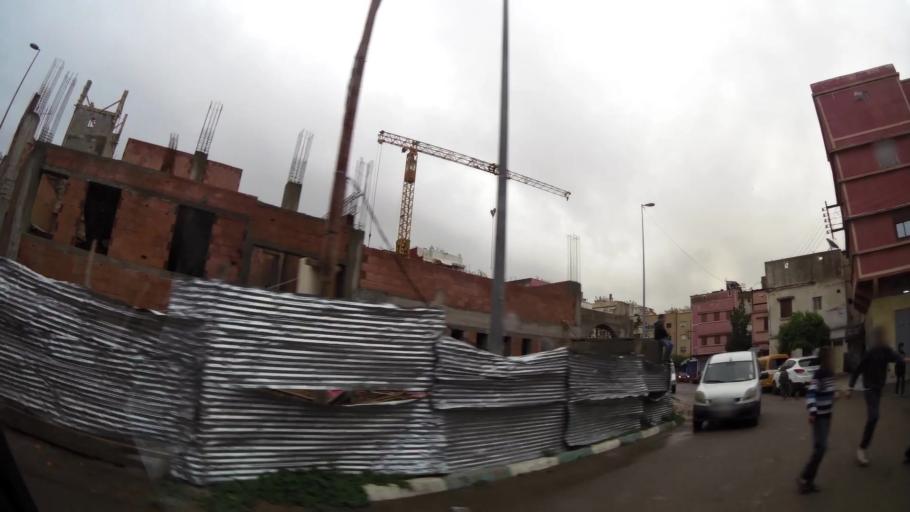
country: MA
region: Grand Casablanca
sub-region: Casablanca
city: Casablanca
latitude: 33.5560
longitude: -7.5860
